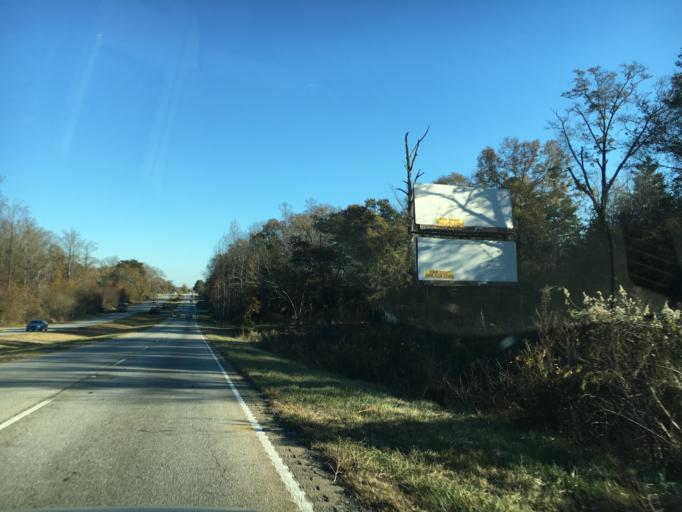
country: US
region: South Carolina
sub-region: Spartanburg County
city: Wellford
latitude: 34.9480
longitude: -82.0987
